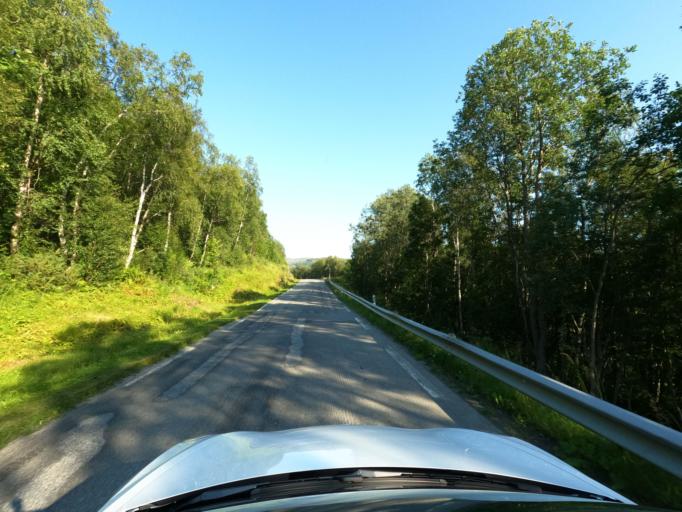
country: NO
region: Nordland
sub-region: Narvik
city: Bjerkvik
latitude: 68.5532
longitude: 17.5753
